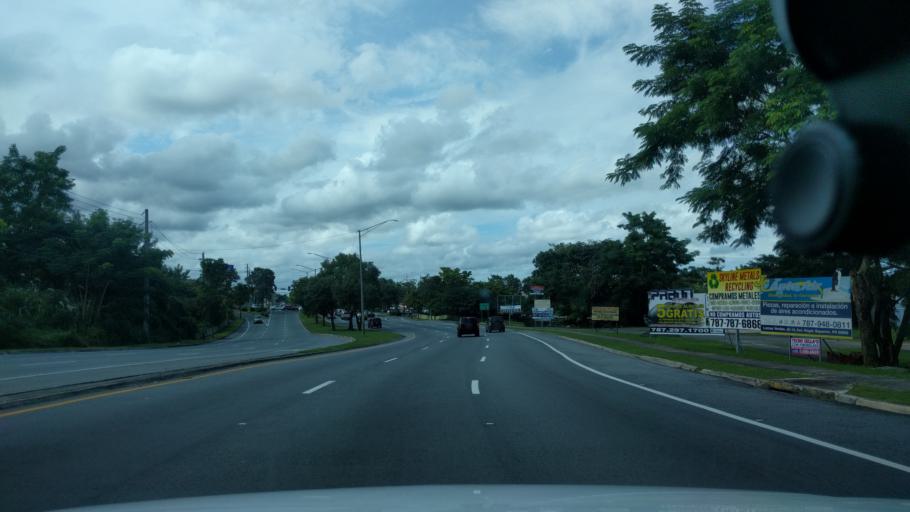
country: PR
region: Toa Alta
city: Pajaros
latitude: 18.3641
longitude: -66.1865
